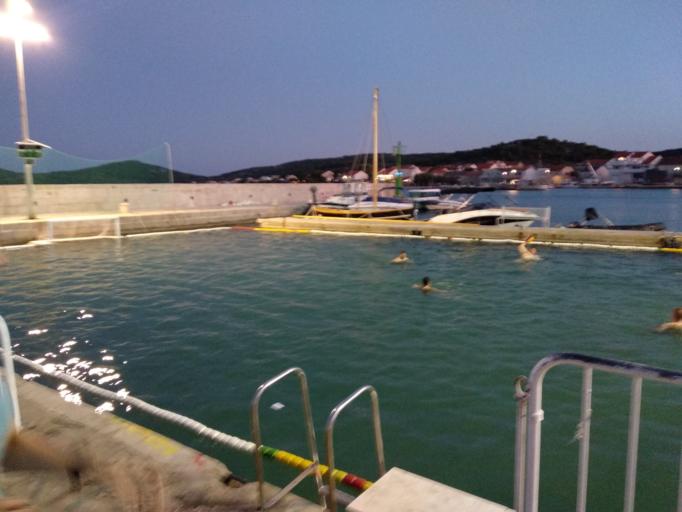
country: HR
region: Sibensko-Kniniska
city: Murter
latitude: 43.8225
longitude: 15.6051
